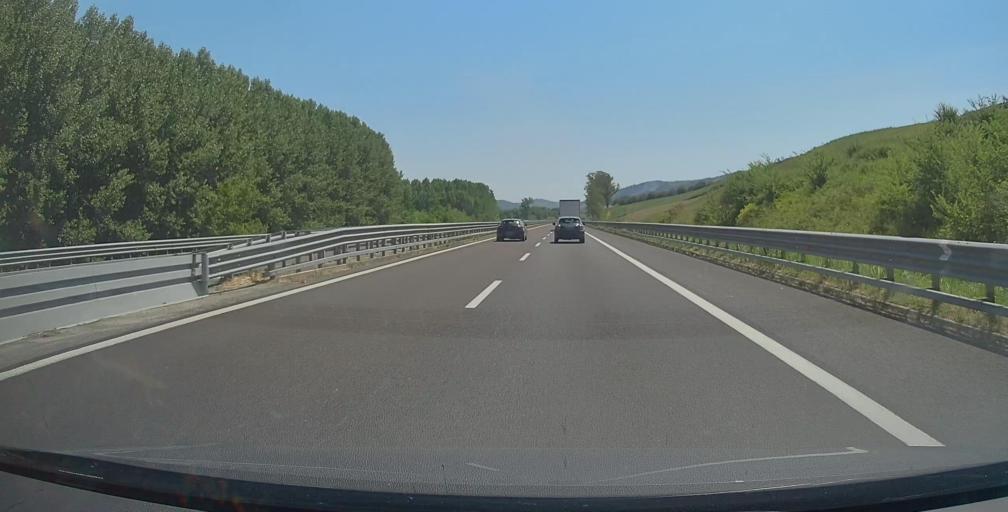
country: IT
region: Calabria
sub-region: Provincia di Vibo-Valentia
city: Francica
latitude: 38.6082
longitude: 16.1486
